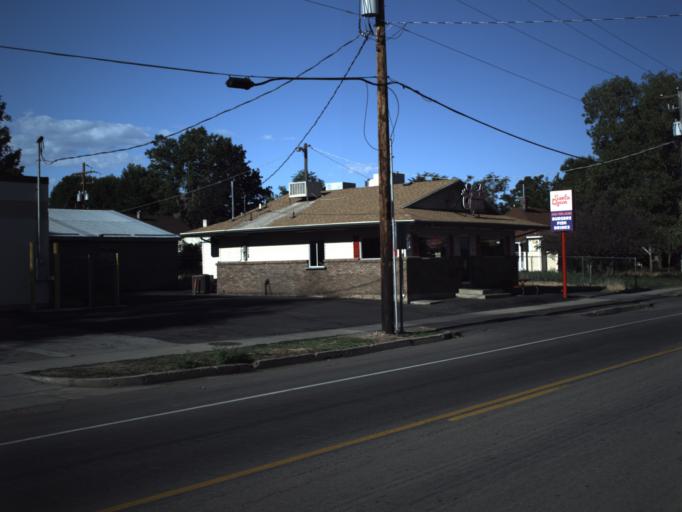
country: US
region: Utah
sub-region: Utah County
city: Santaquin
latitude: 39.9756
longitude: -111.7841
